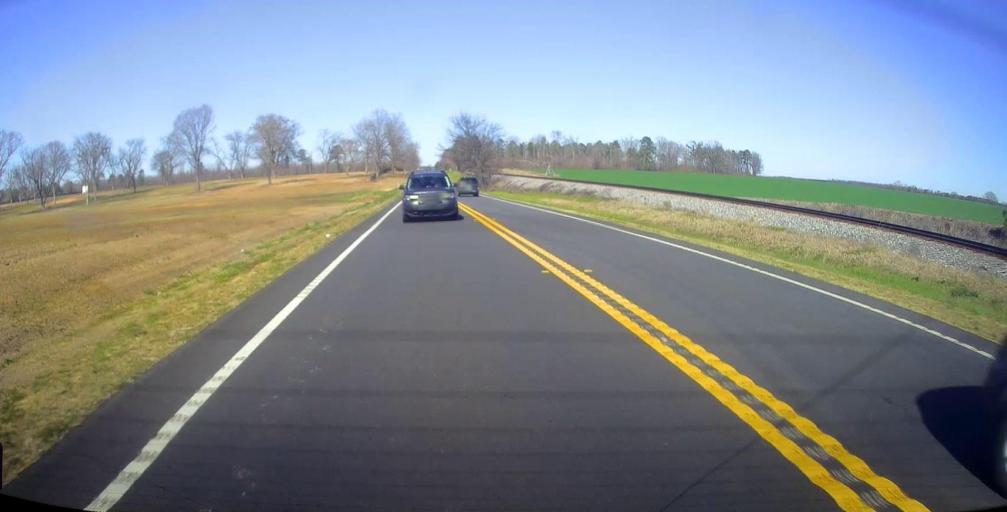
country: US
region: Georgia
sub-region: Macon County
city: Marshallville
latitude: 32.4745
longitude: -83.9345
